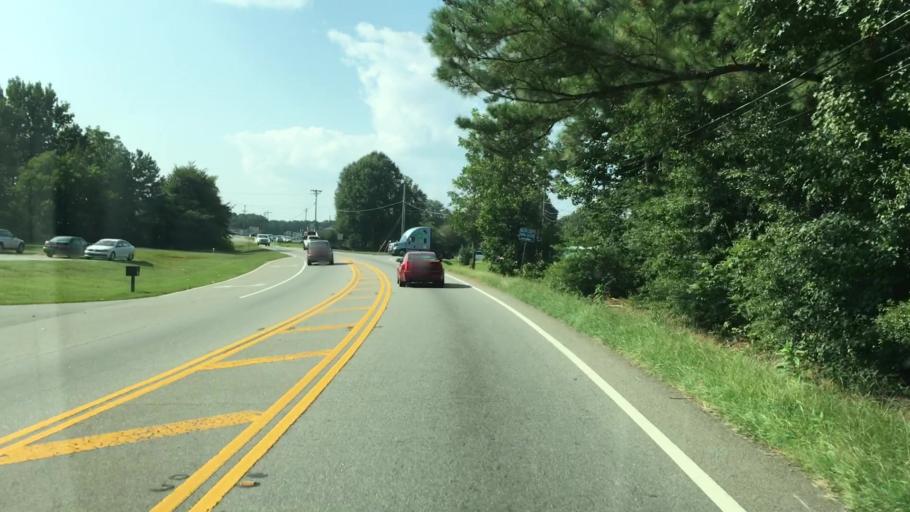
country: US
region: Georgia
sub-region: Walton County
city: Monroe
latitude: 33.7695
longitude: -83.7001
